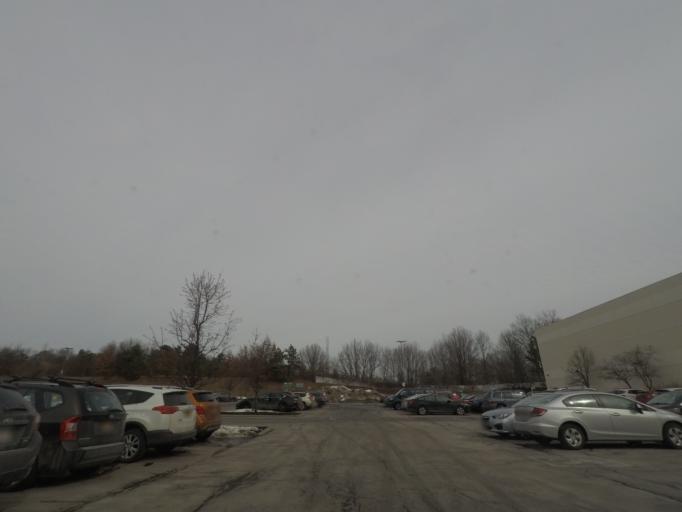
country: US
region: New York
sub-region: Albany County
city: McKownville
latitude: 42.6914
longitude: -73.8530
